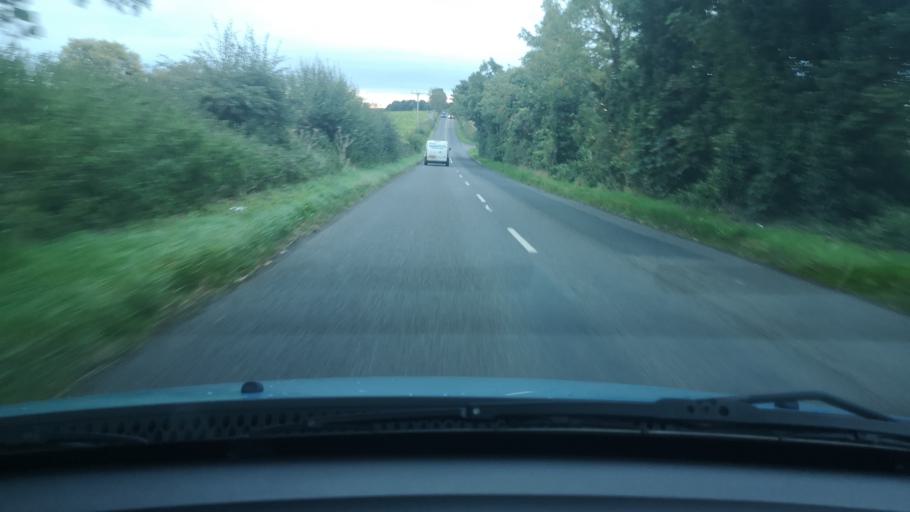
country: GB
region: England
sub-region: Doncaster
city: Campsall
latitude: 53.6173
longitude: -1.1983
